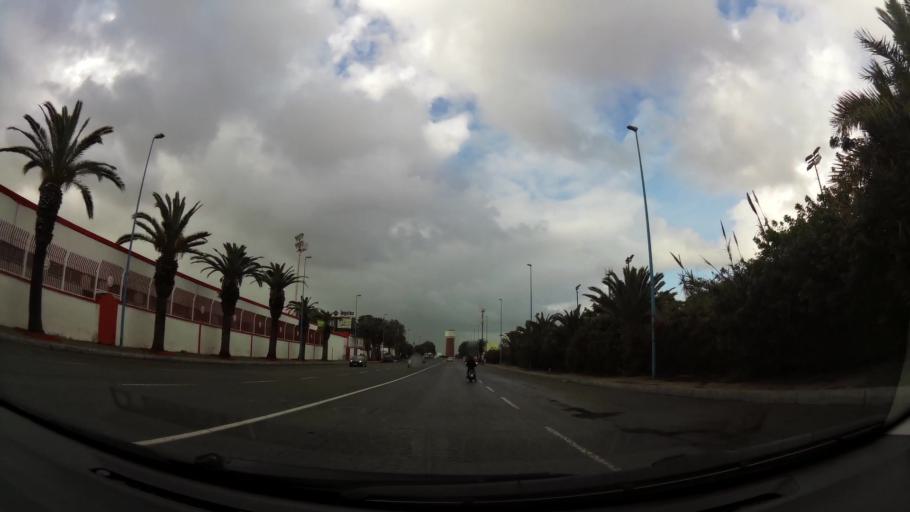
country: MA
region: Grand Casablanca
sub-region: Casablanca
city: Casablanca
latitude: 33.5600
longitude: -7.6479
